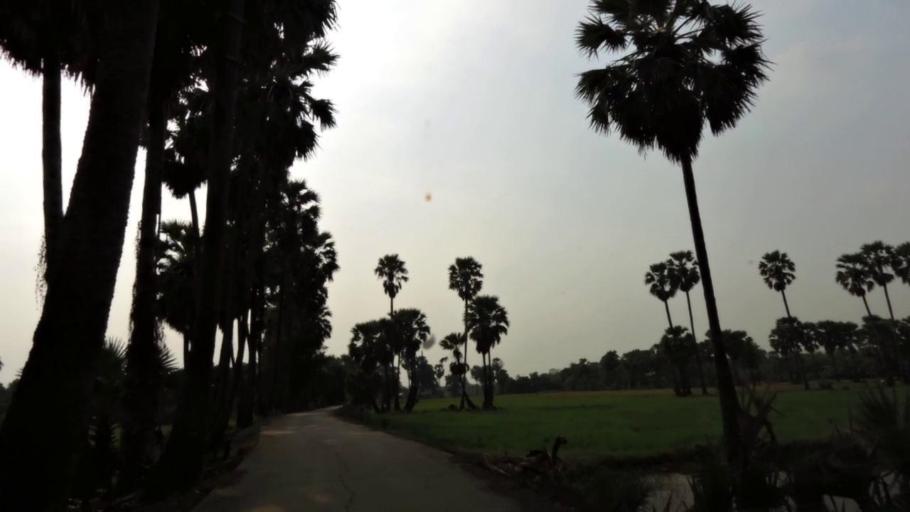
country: TH
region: Phra Nakhon Si Ayutthaya
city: Phra Nakhon Si Ayutthaya
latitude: 14.3415
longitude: 100.5718
